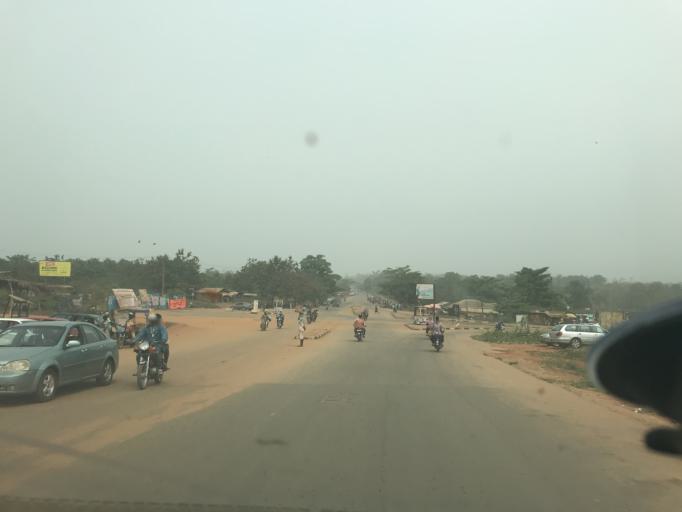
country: NG
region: Ogun
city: Ilaro
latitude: 6.8967
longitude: 3.0217
